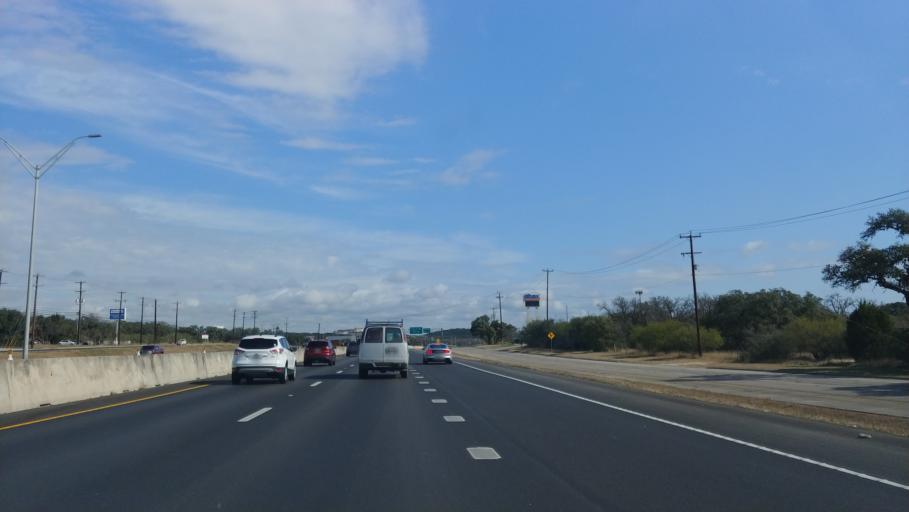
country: US
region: Texas
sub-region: Bexar County
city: Helotes
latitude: 29.5820
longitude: -98.6403
